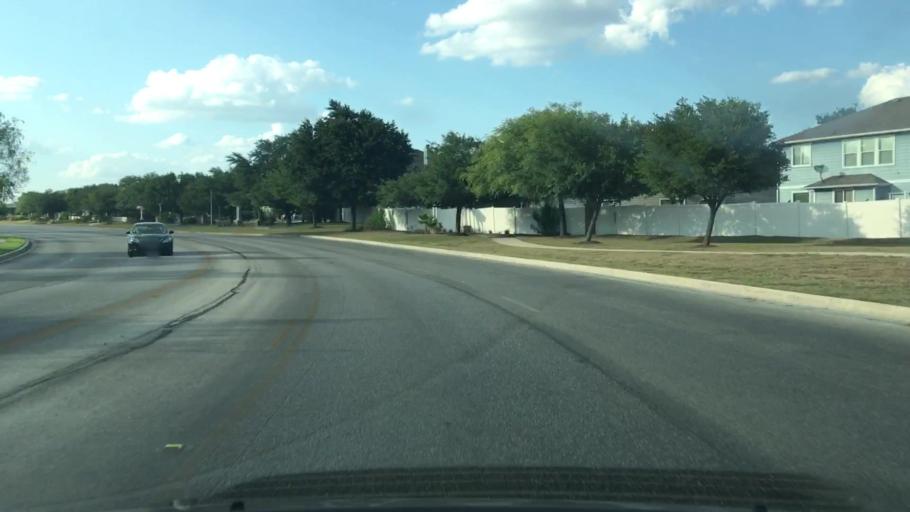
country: US
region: Texas
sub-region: Guadalupe County
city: Cibolo
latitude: 29.5897
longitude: -98.2491
